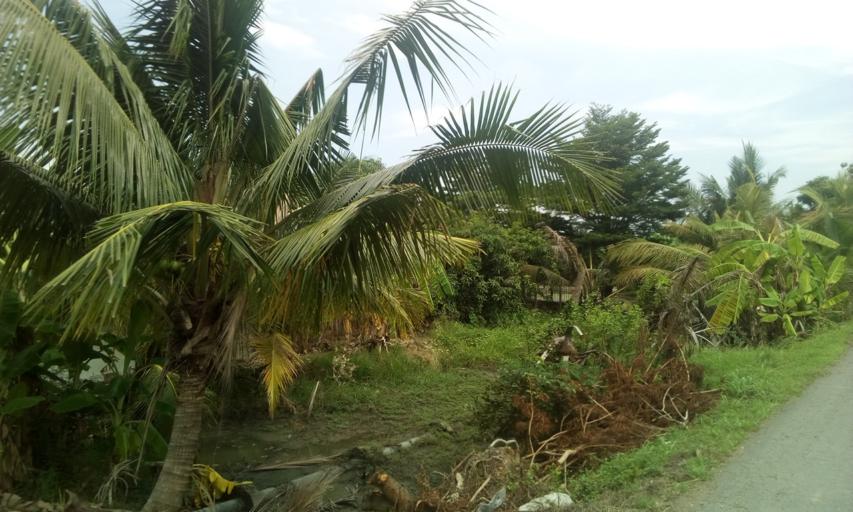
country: TH
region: Pathum Thani
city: Ban Lam Luk Ka
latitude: 14.0112
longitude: 100.8426
